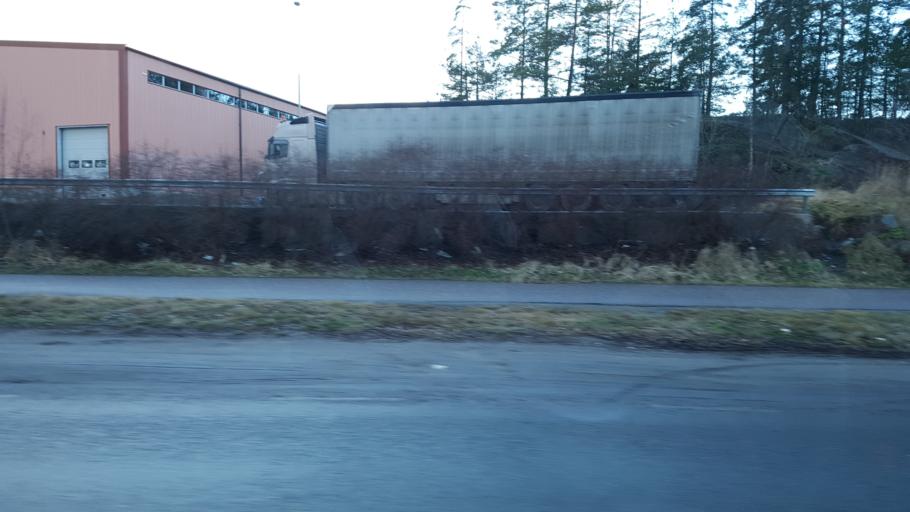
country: SE
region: Stockholm
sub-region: Tyreso Kommun
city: Bollmora
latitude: 59.2415
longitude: 18.2154
